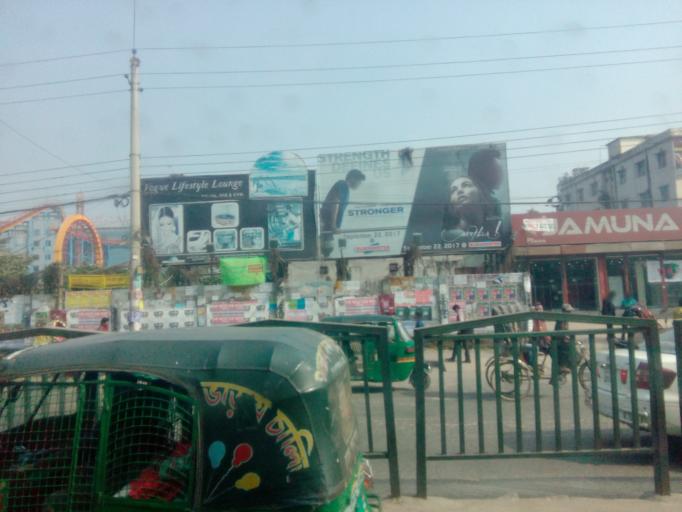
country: BD
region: Dhaka
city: Paltan
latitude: 23.8122
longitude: 90.4213
